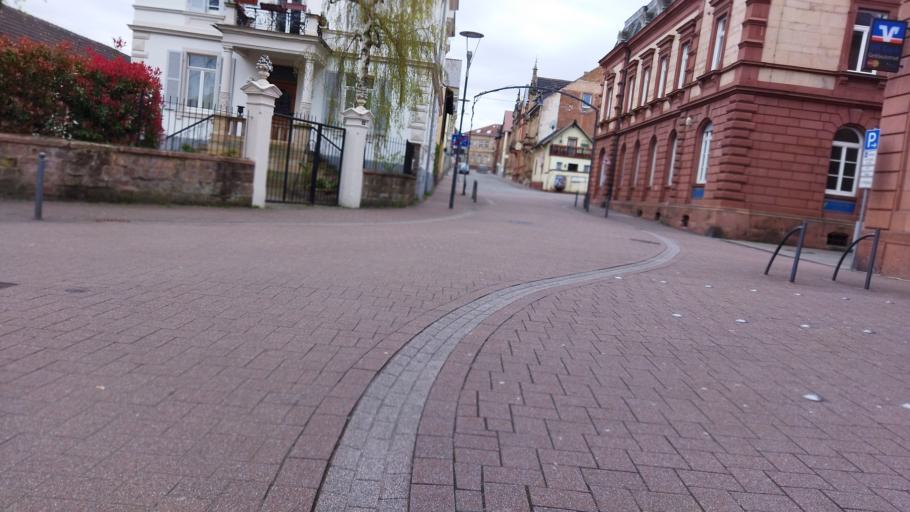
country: DE
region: Rheinland-Pfalz
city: Edenkoben
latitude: 49.2803
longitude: 8.1254
